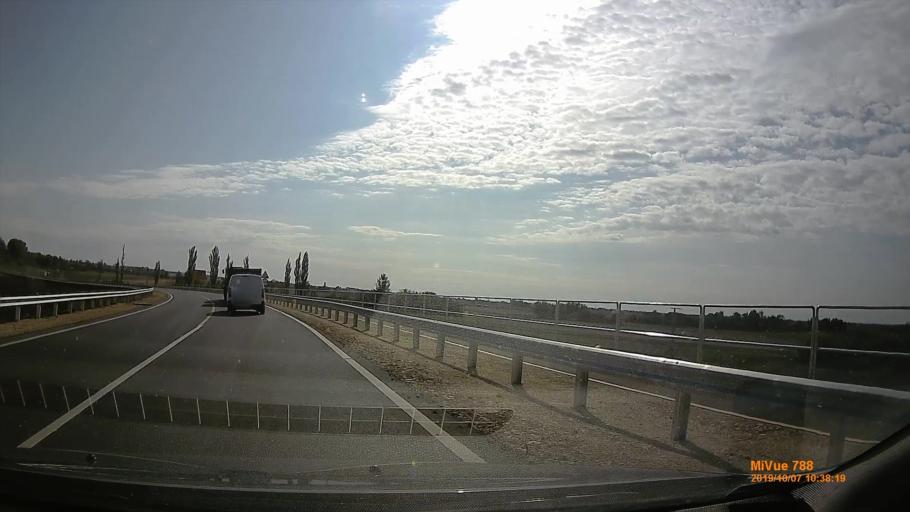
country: HU
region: Bekes
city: Kondoros
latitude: 46.7456
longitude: 20.8531
